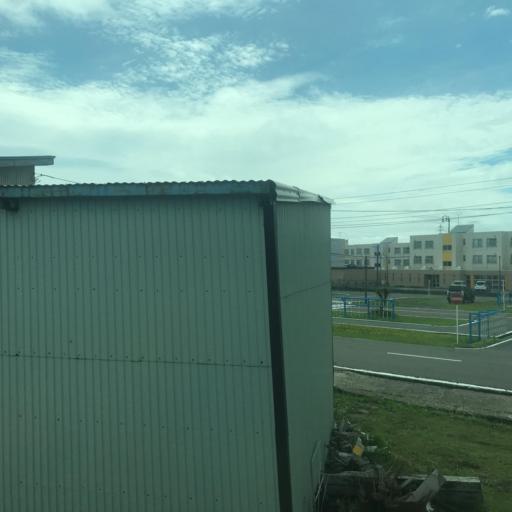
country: JP
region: Aomori
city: Goshogawara
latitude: 40.7949
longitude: 140.4449
